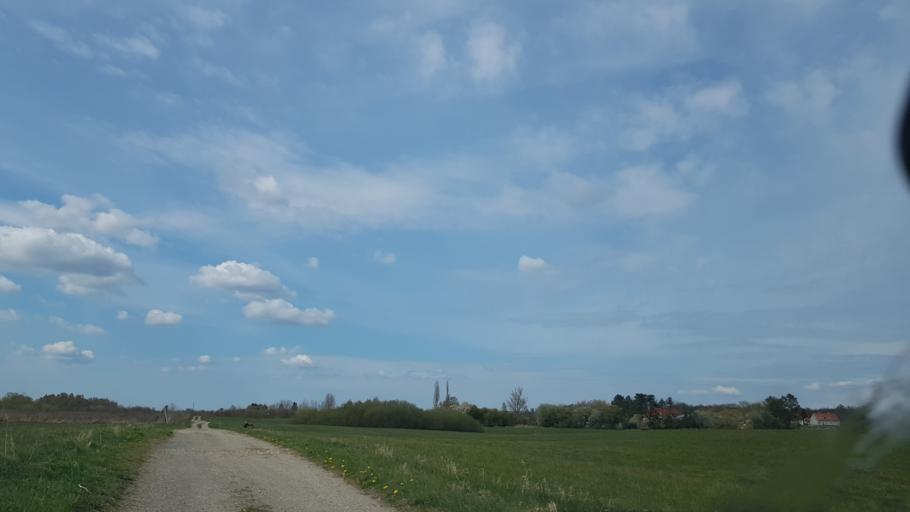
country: DK
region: Capital Region
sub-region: Allerod Kommune
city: Lillerod
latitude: 55.8959
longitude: 12.3370
